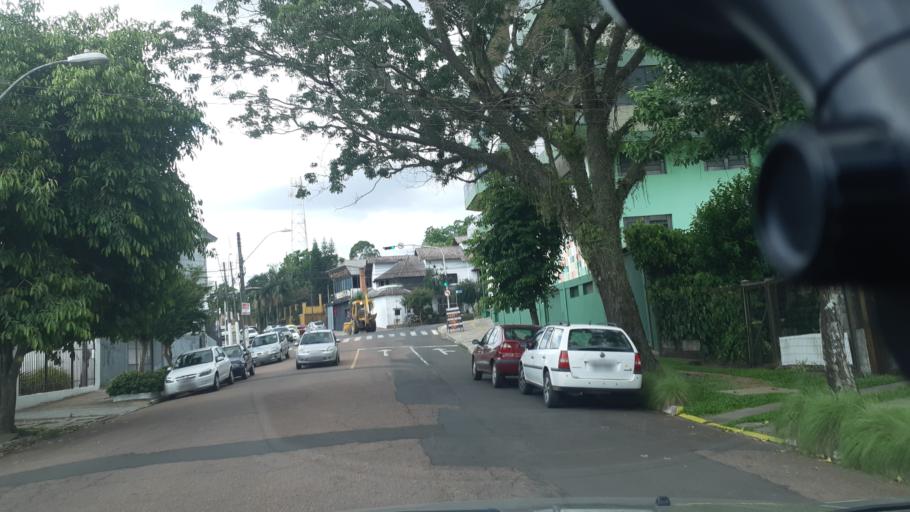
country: BR
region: Rio Grande do Sul
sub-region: Esteio
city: Esteio
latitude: -29.8497
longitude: -51.1679
